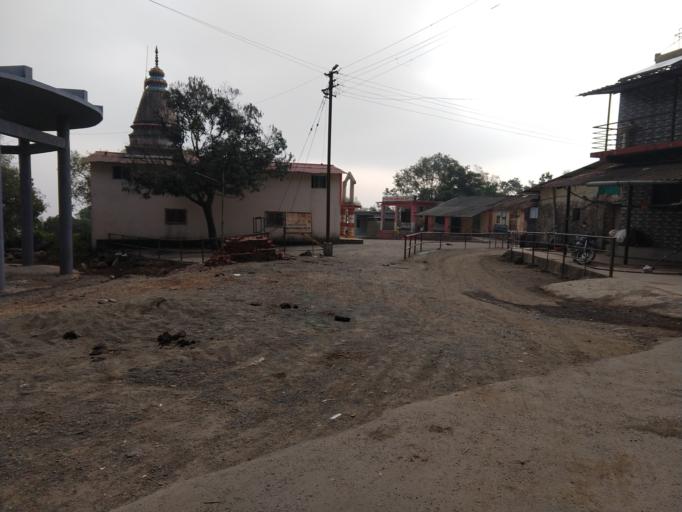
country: IN
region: Maharashtra
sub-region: Pune Division
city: Lonavla
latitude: 18.7095
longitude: 73.4796
